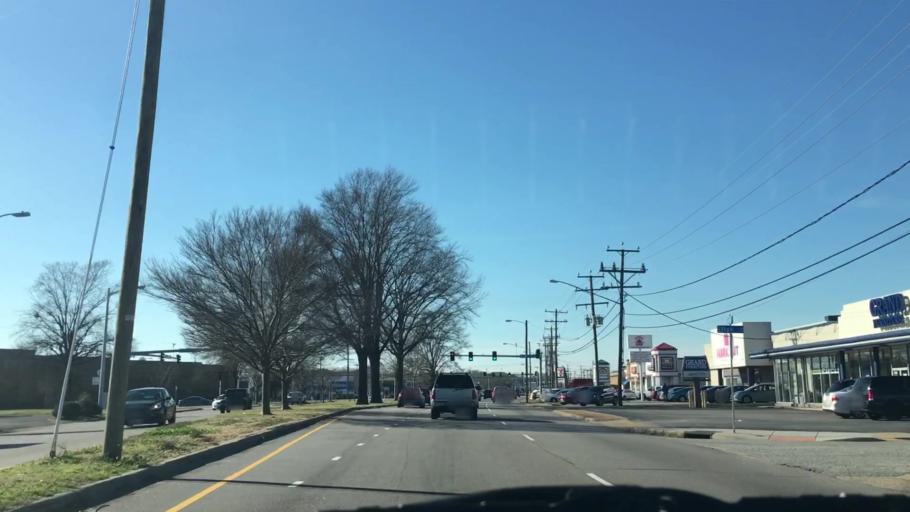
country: US
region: Virginia
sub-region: City of Norfolk
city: Norfolk
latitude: 36.9153
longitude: -76.2492
